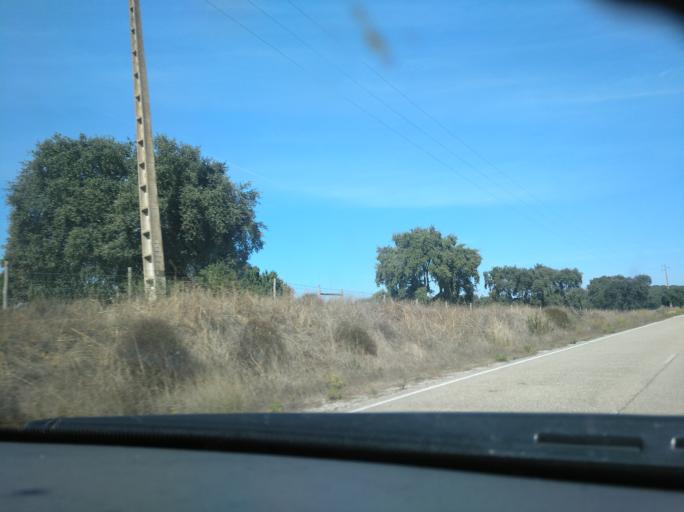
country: PT
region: Evora
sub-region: Arraiolos
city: Arraiolos
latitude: 38.6818
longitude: -8.0920
